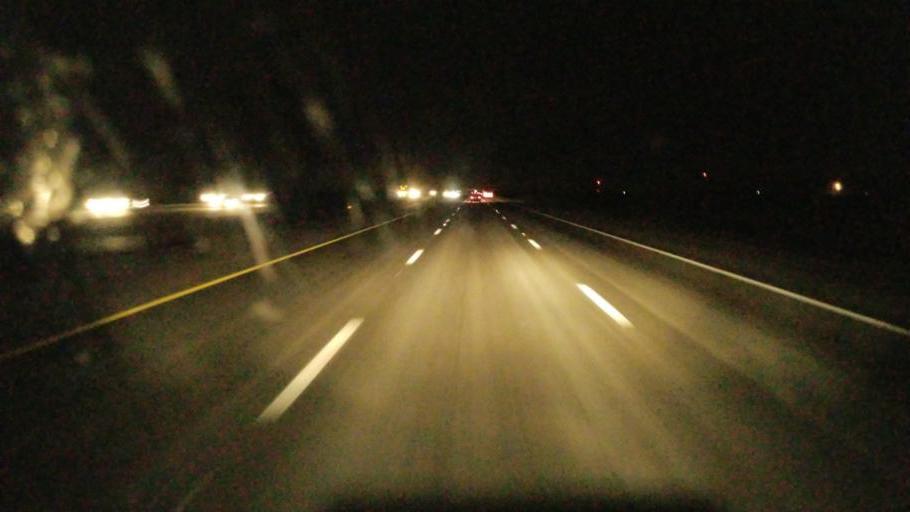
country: US
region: Ohio
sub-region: Madison County
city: Choctaw Lake
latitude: 39.9421
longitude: -83.4630
